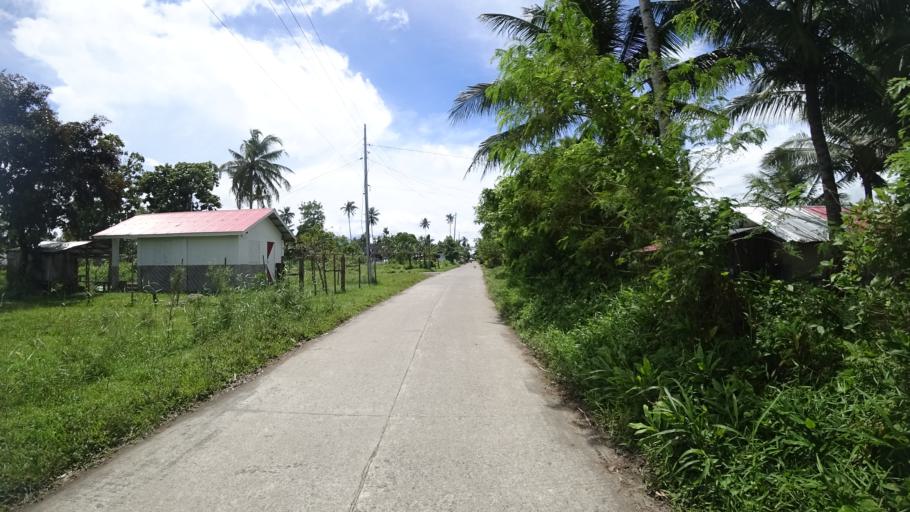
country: PH
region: Eastern Visayas
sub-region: Province of Leyte
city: Alangalang
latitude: 11.2302
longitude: 124.8442
